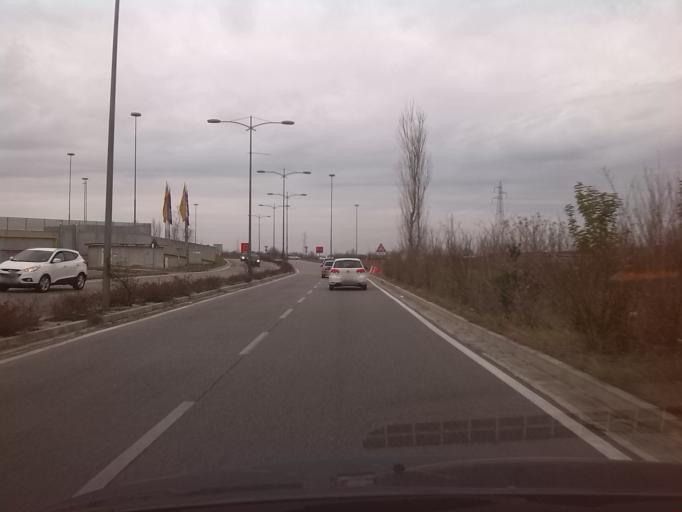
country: IT
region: Friuli Venezia Giulia
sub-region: Provincia di Gorizia
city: Villesse
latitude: 45.8659
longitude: 13.4349
